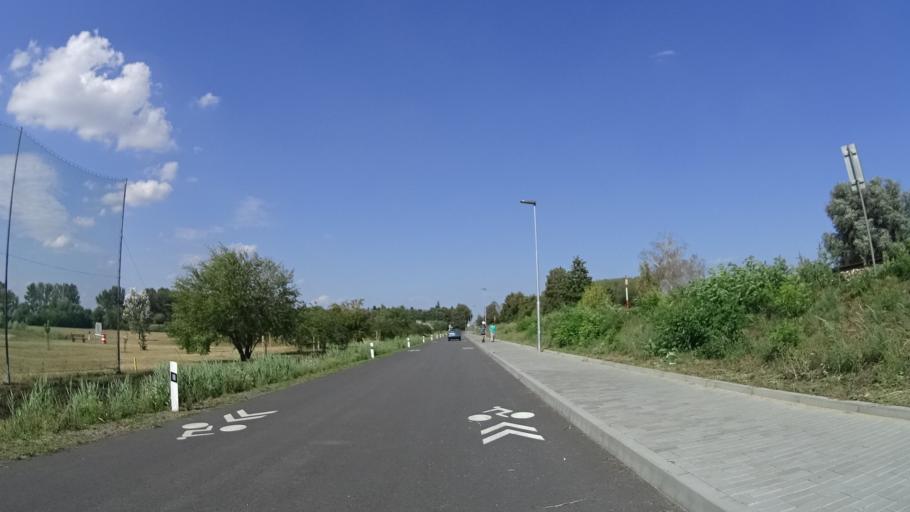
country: CZ
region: Zlin
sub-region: Okres Zlin
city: Ostrozska Nova Ves
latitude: 49.0139
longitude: 17.4413
